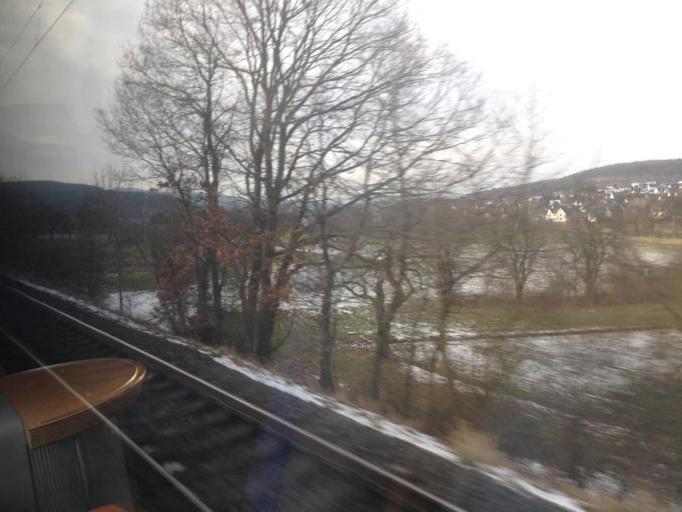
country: DE
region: Hesse
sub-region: Regierungsbezirk Giessen
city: Ehringshausen
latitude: 50.6144
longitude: 8.3506
